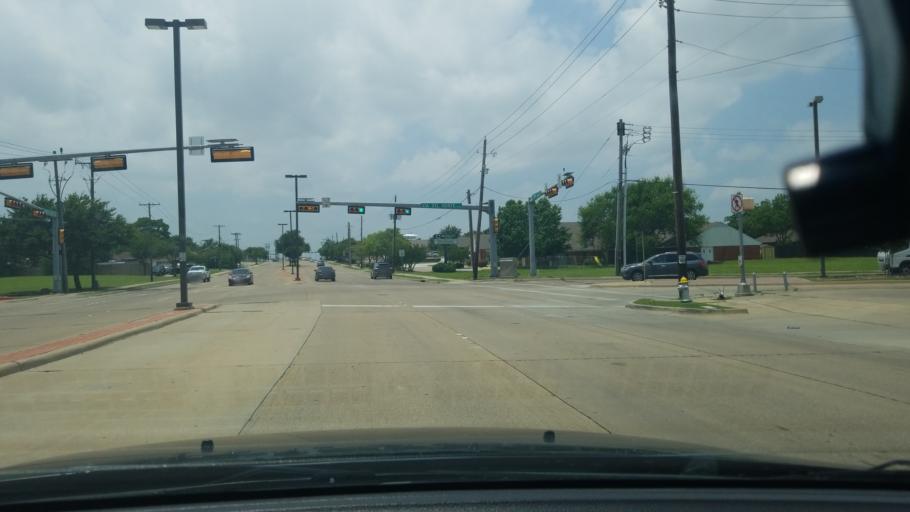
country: US
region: Texas
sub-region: Dallas County
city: Mesquite
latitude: 32.8136
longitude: -96.6068
